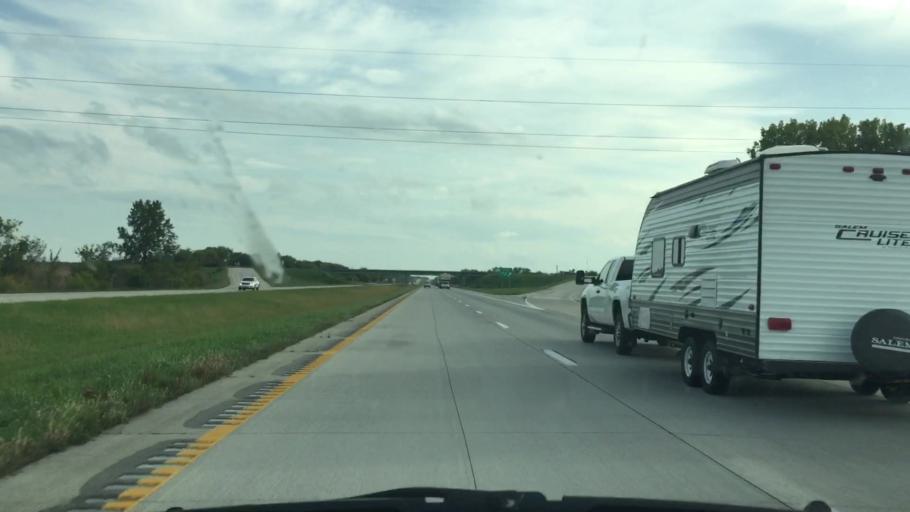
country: US
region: Missouri
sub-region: Daviess County
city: Gallatin
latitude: 40.0001
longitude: -94.0961
